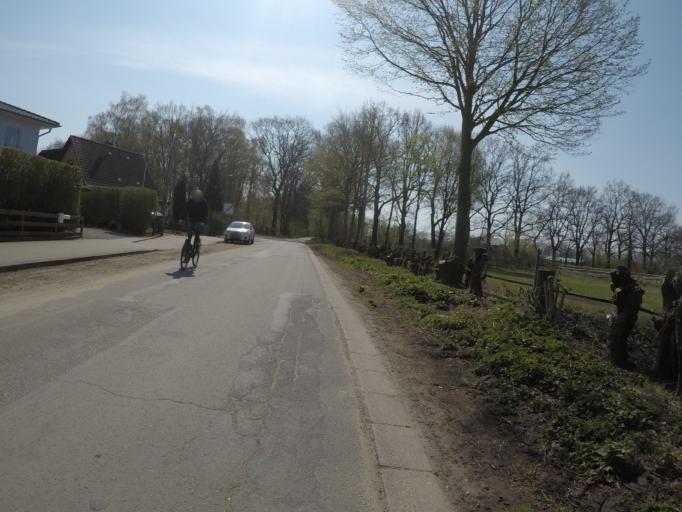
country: DE
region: Schleswig-Holstein
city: Rellingen
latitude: 53.6007
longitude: 9.8109
